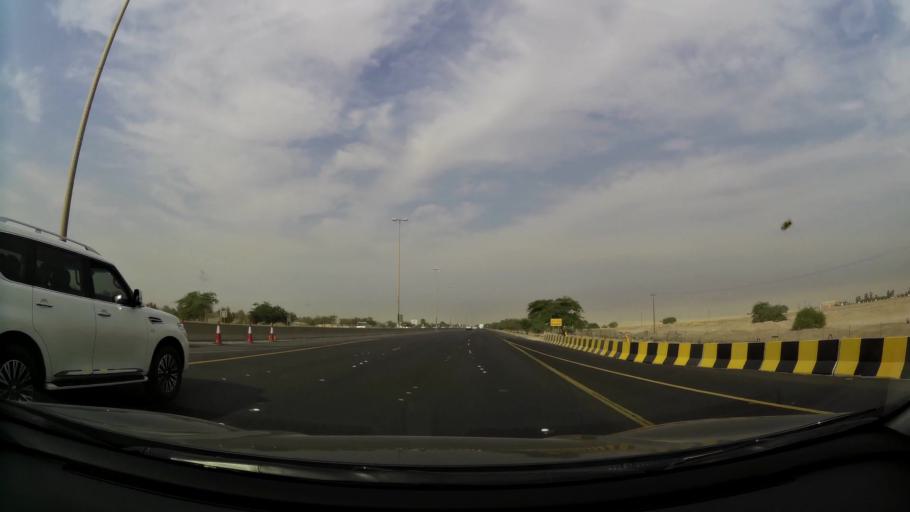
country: KW
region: Muhafazat al Jahra'
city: Al Jahra'
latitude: 29.2860
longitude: 47.7780
